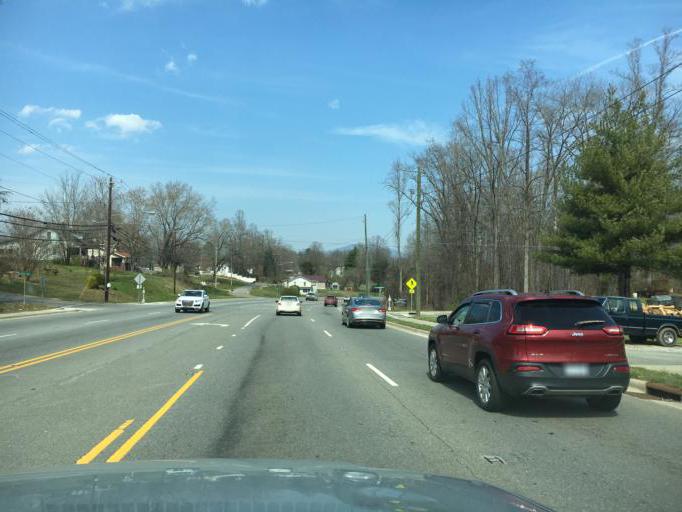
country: US
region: North Carolina
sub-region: McDowell County
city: West Marion
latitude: 35.6695
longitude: -82.0185
